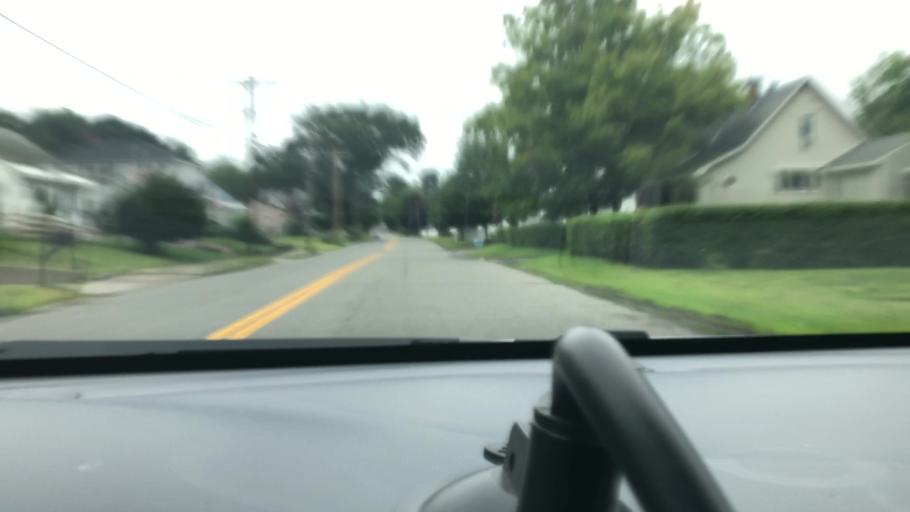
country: US
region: New Hampshire
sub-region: Hillsborough County
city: Pinardville
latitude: 42.9846
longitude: -71.4952
